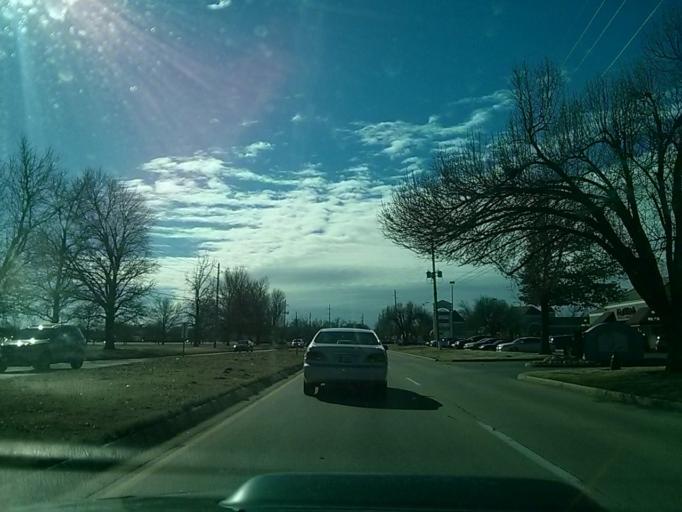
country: US
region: Oklahoma
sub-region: Tulsa County
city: Jenks
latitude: 36.0454
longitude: -95.9579
